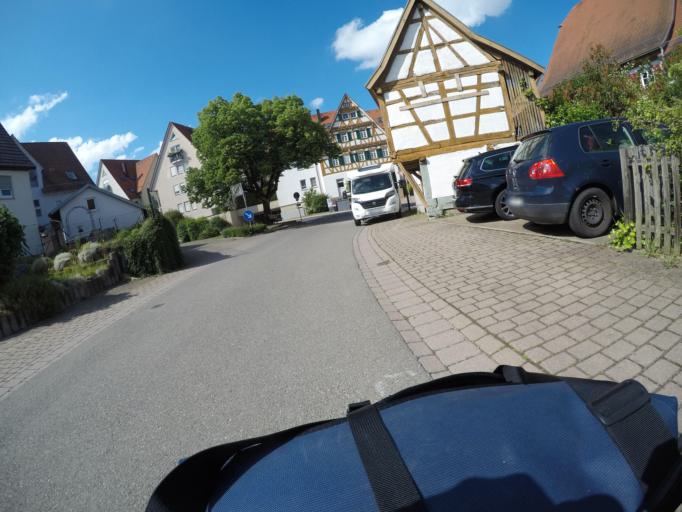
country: DE
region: Baden-Wuerttemberg
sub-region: Regierungsbezirk Stuttgart
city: Herrenberg
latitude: 48.6108
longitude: 8.8399
